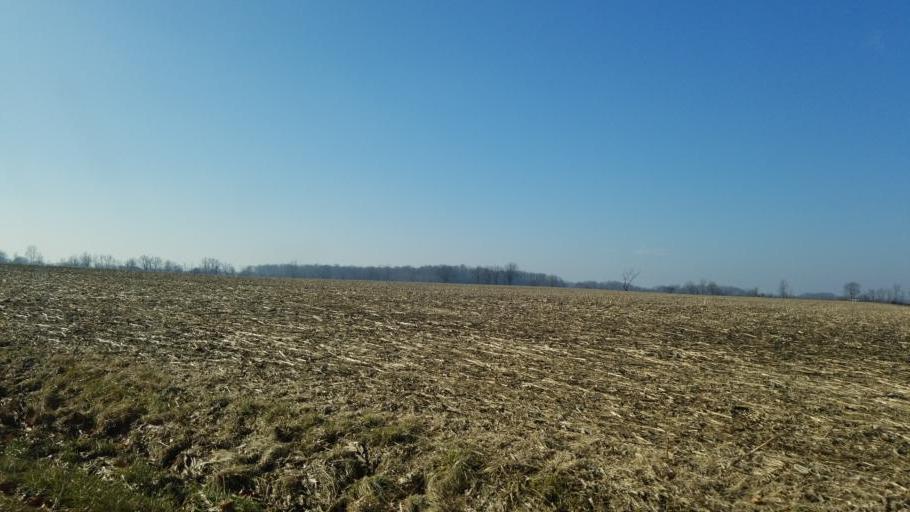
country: US
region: Ohio
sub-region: Seneca County
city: Tiffin
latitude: 41.1075
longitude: -83.1120
